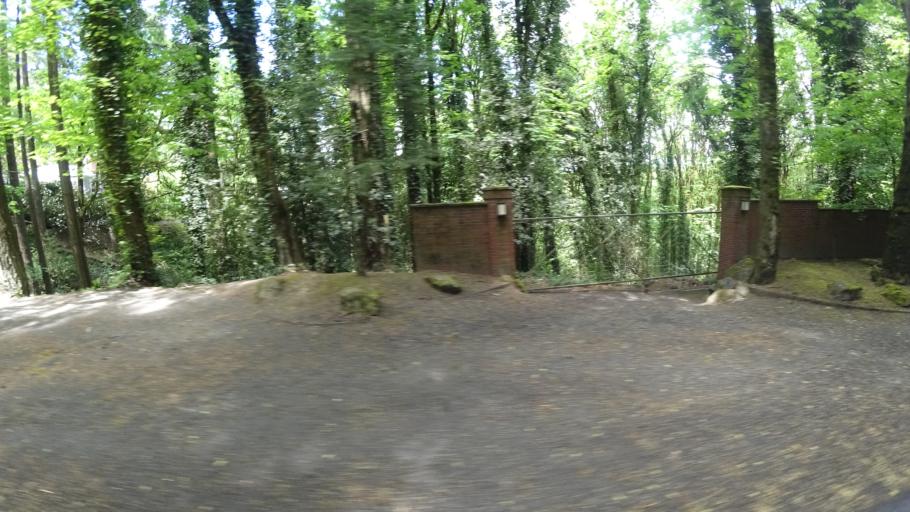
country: US
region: Oregon
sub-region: Washington County
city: West Slope
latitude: 45.5055
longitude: -122.7227
